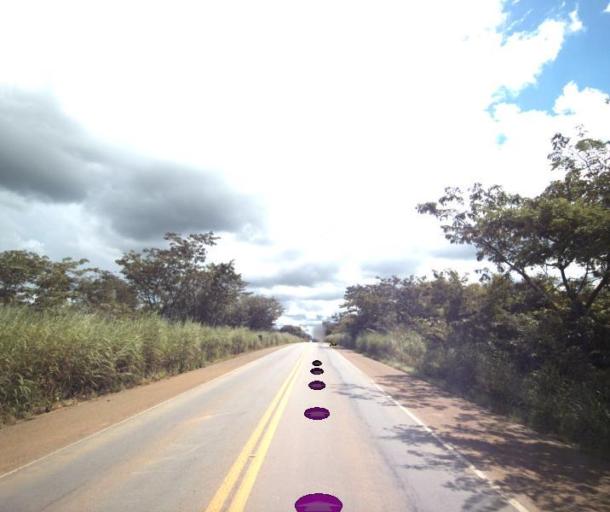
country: BR
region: Goias
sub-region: Pirenopolis
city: Pirenopolis
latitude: -16.0897
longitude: -49.0378
